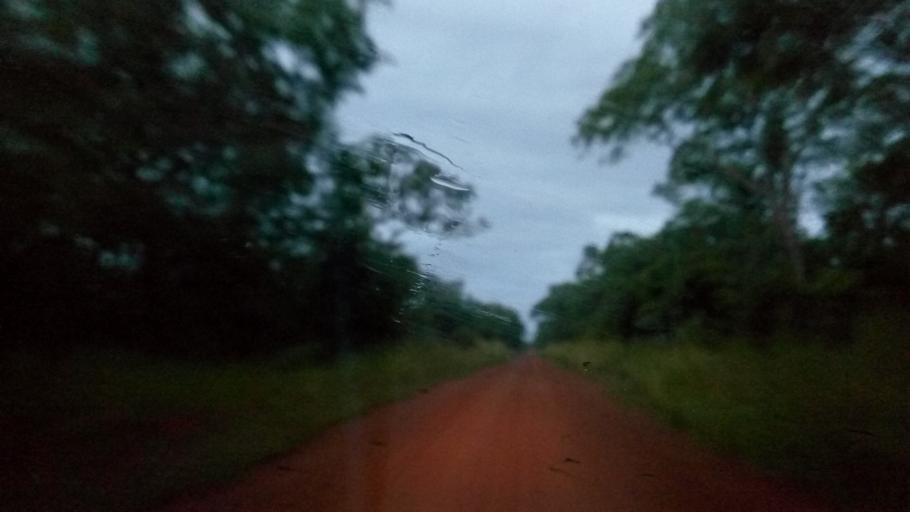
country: ZM
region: Luapula
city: Nchelenge
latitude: -9.8239
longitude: 28.1348
